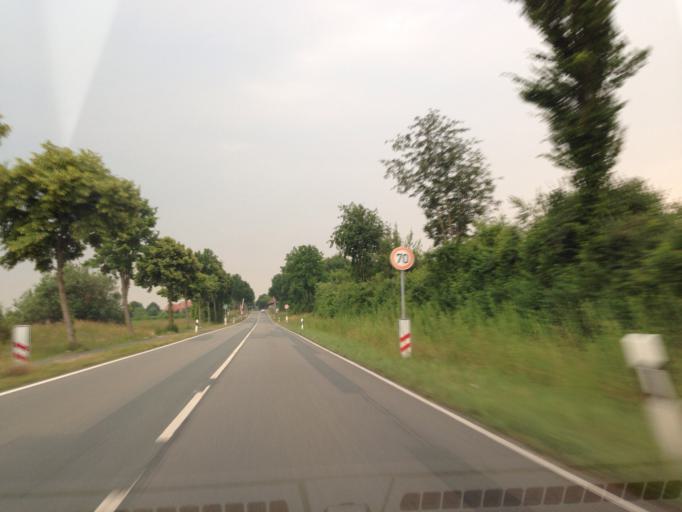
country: DE
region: North Rhine-Westphalia
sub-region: Regierungsbezirk Munster
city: Havixbeck
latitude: 51.9608
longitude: 7.4258
